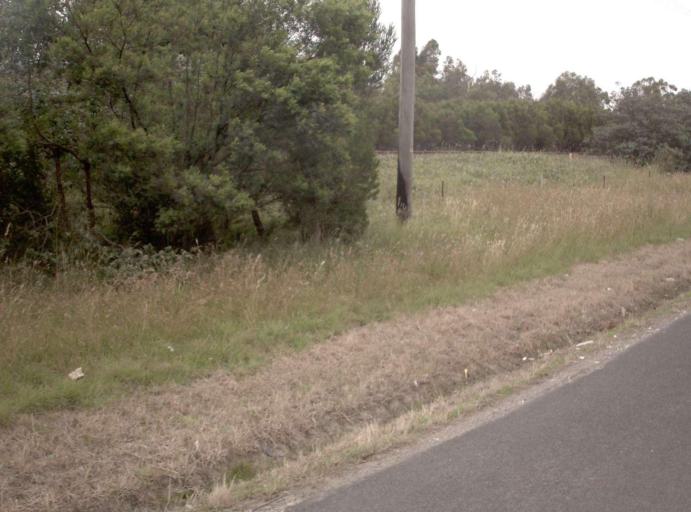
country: AU
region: Victoria
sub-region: Latrobe
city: Traralgon
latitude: -38.2139
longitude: 146.4823
